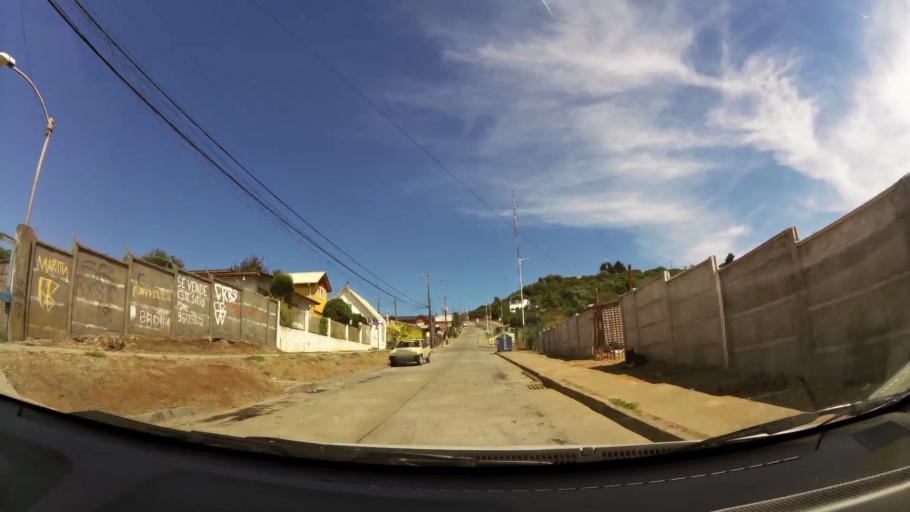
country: CL
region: Biobio
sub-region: Provincia de Concepcion
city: Talcahuano
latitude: -36.7080
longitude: -73.1200
